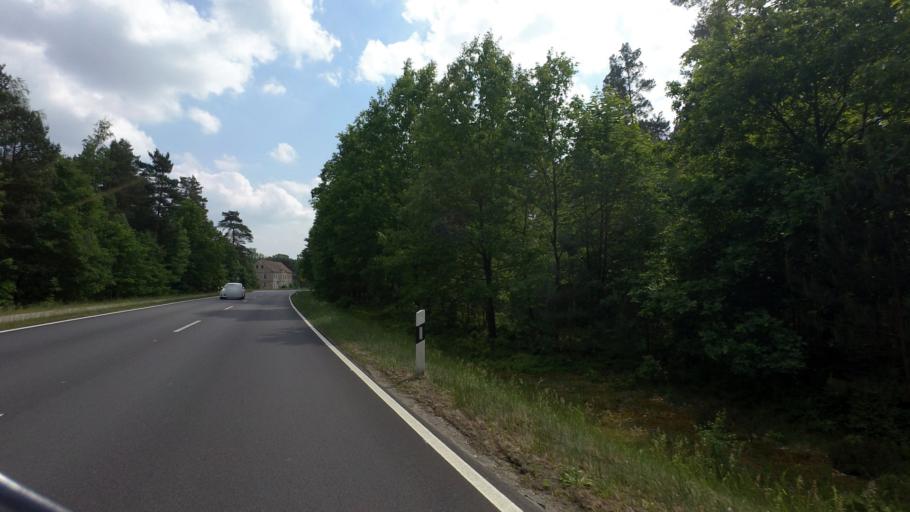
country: DE
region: Saxony
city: Niesky
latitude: 51.3383
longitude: 14.8106
